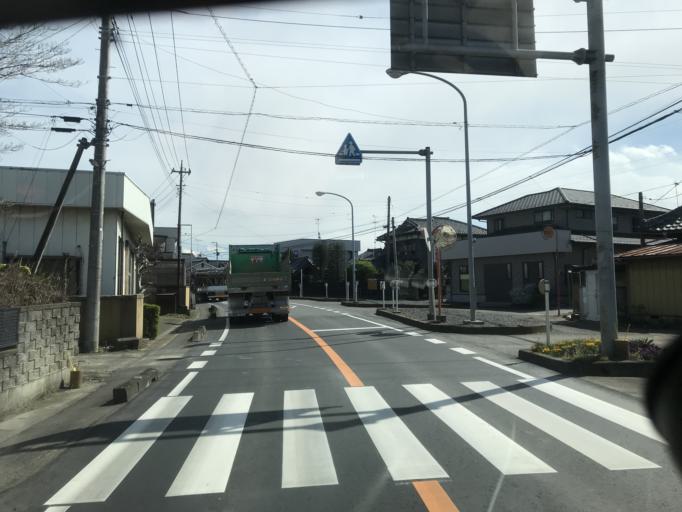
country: JP
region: Ibaraki
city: Yuki
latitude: 36.2489
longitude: 139.9157
